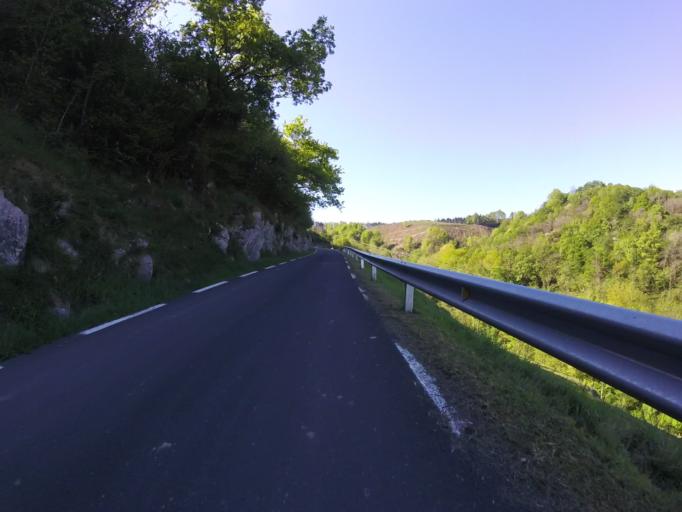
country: ES
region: Basque Country
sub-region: Provincia de Guipuzcoa
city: Aizarnazabal
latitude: 43.2225
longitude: -2.2128
